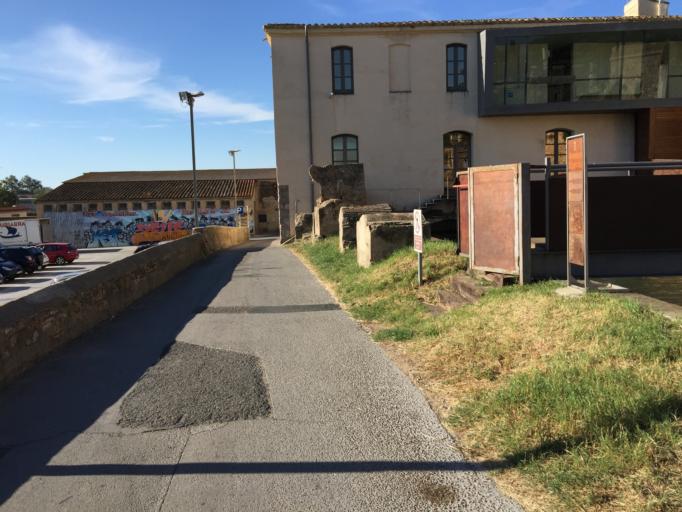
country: ES
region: Catalonia
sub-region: Provincia de Girona
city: Castello d'Empuries
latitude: 42.2592
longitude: 3.0770
